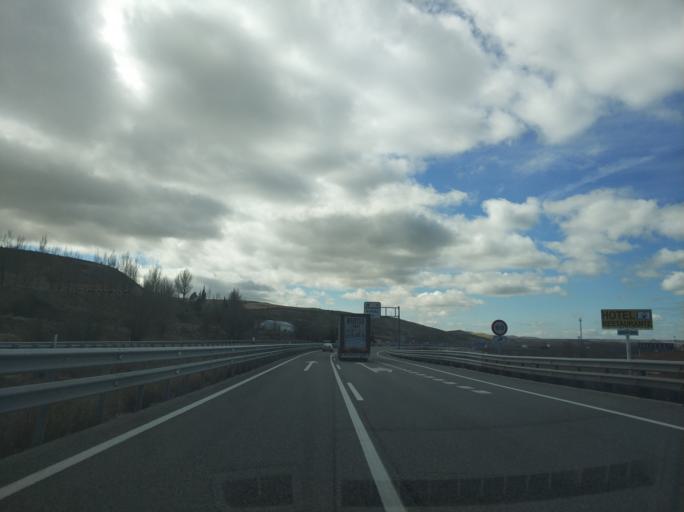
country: ES
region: Castille and Leon
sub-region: Provincia de Burgos
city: Buniel
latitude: 42.3069
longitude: -3.8231
